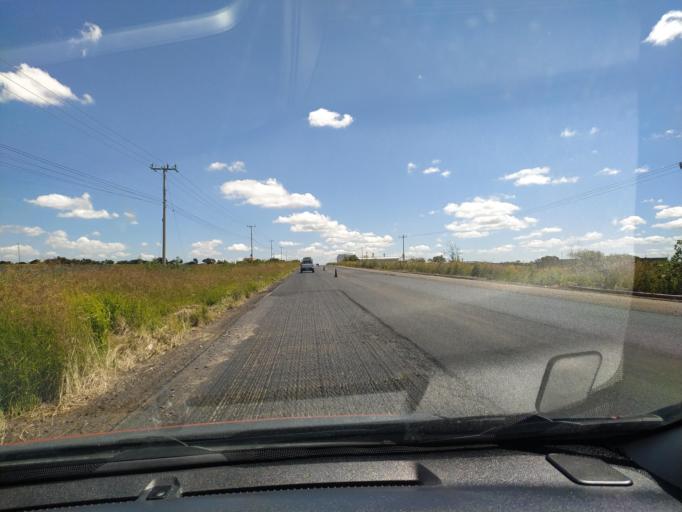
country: MX
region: Jalisco
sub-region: San Julian
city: Colonia Veintitres de Mayo
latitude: 21.0107
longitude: -102.2253
